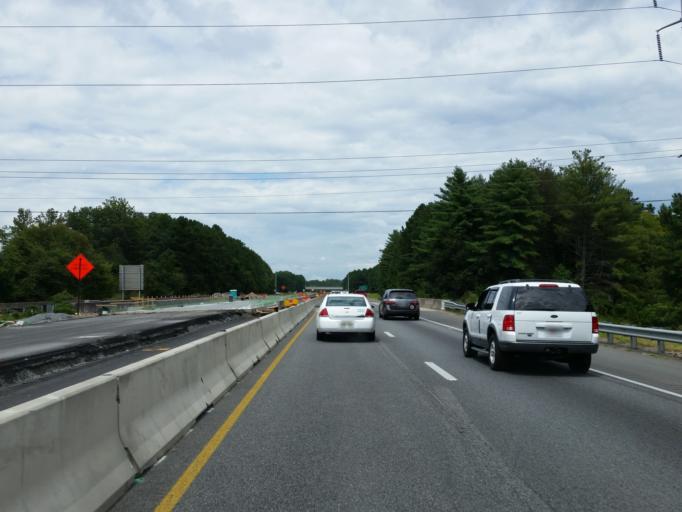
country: US
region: Georgia
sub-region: Cobb County
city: Kennesaw
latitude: 34.0286
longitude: -84.5605
